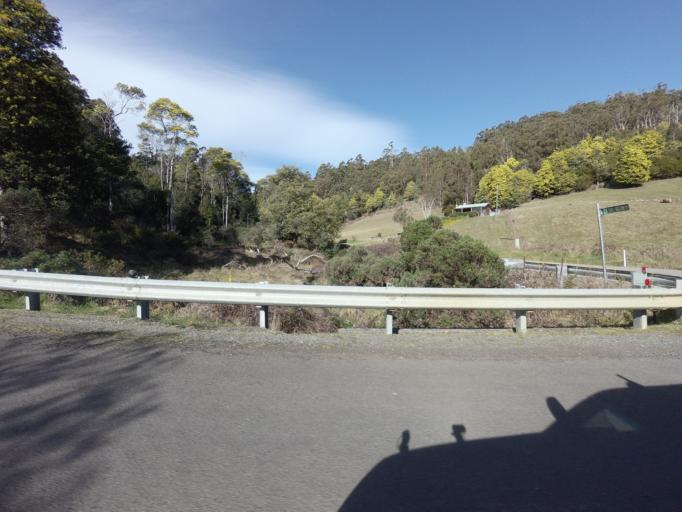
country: AU
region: Tasmania
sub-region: Huon Valley
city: Cygnet
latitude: -43.1746
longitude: 147.1569
